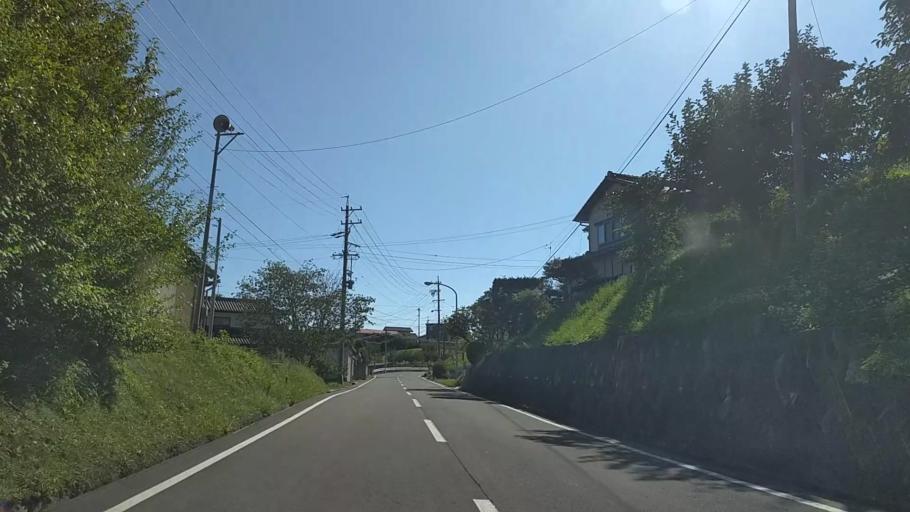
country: JP
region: Nagano
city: Nagano-shi
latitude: 36.5786
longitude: 138.1191
